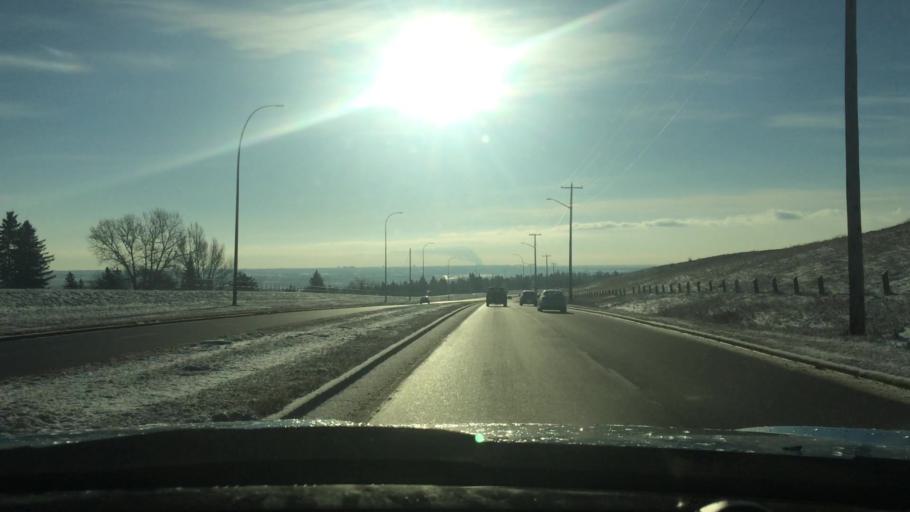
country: CA
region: Alberta
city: Calgary
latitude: 51.1193
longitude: -114.0892
